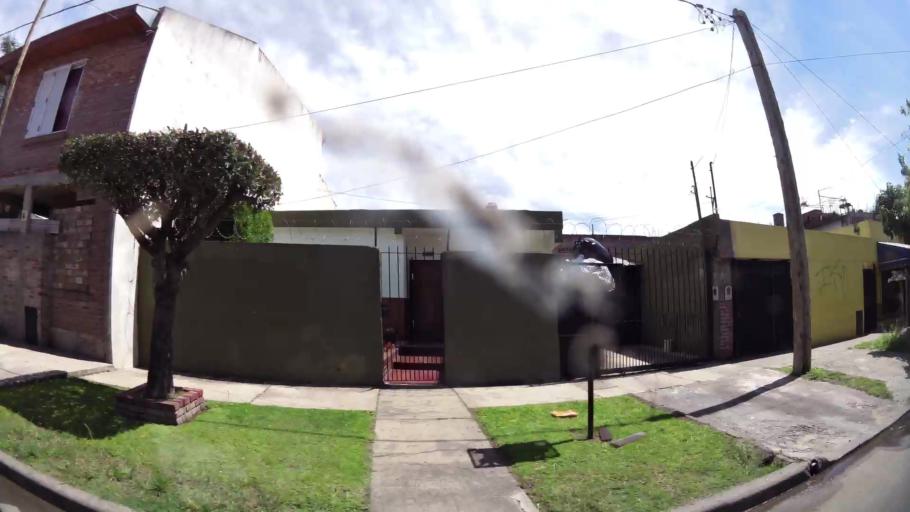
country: AR
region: Buenos Aires
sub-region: Partido de Quilmes
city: Quilmes
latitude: -34.7457
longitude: -58.2950
